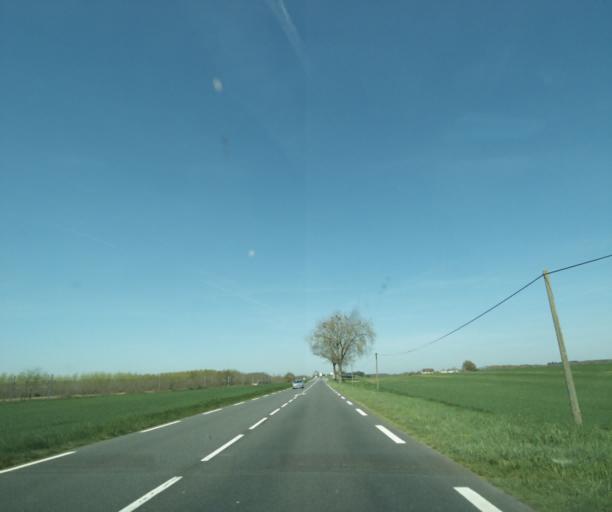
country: FR
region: Auvergne
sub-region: Departement de l'Allier
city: Trevol
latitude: 46.6709
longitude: 3.2372
